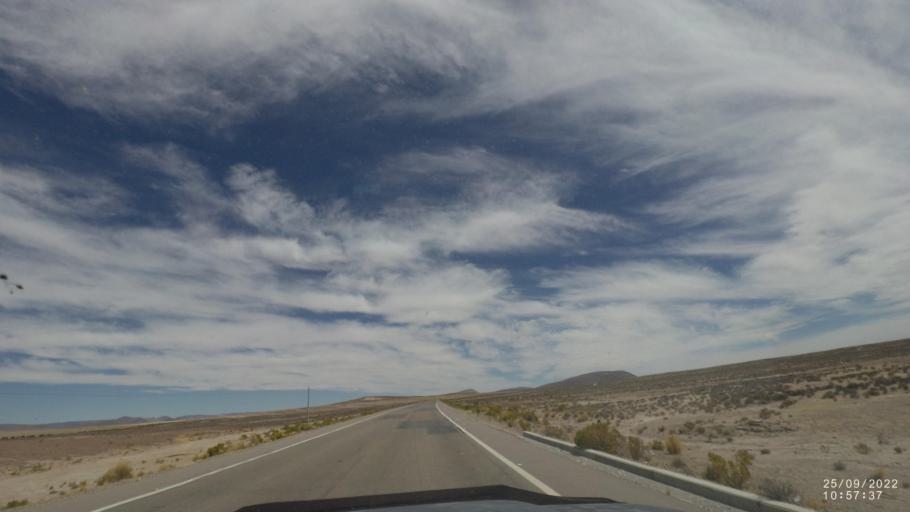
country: BO
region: Oruro
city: Challapata
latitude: -19.4731
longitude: -66.8940
